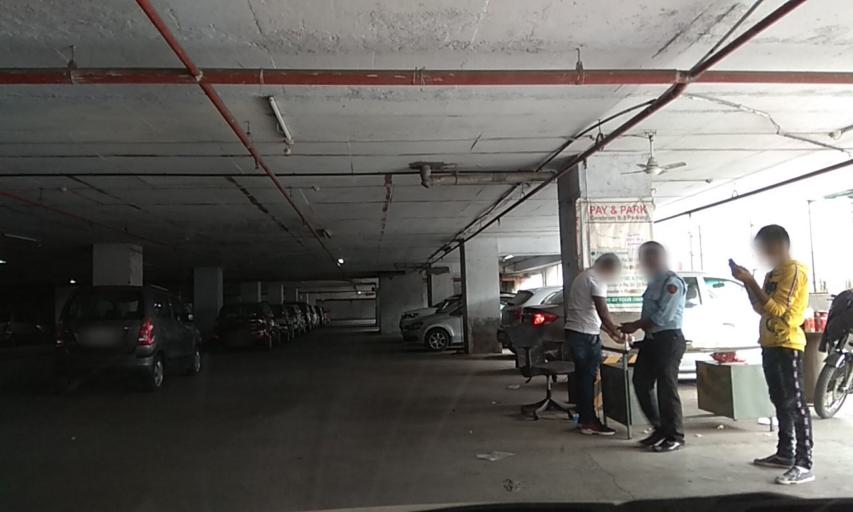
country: IN
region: Maharashtra
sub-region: Pune Division
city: Lohogaon
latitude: 18.5444
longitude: 73.9112
